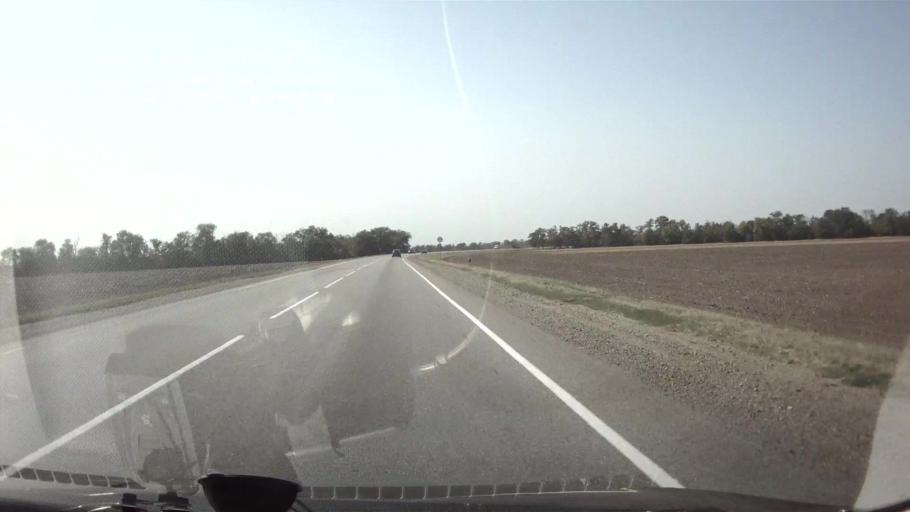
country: RU
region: Krasnodarskiy
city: Tbilisskaya
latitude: 45.4172
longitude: 40.2996
